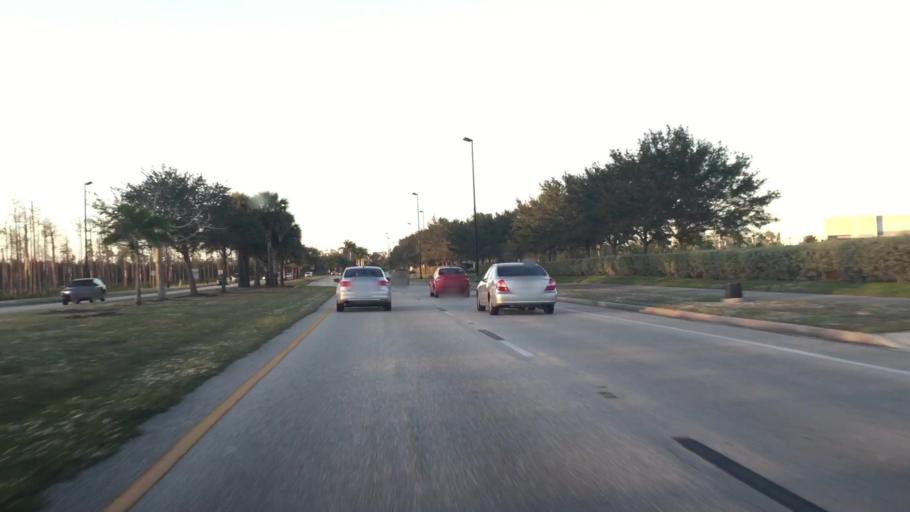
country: US
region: Florida
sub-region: Lee County
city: Three Oaks
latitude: 26.4999
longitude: -81.7842
